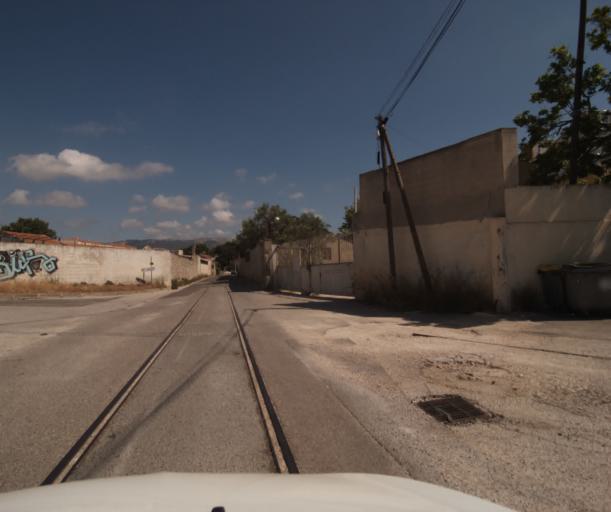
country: FR
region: Provence-Alpes-Cote d'Azur
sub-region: Departement du Var
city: La Seyne-sur-Mer
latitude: 43.1092
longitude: 5.8794
